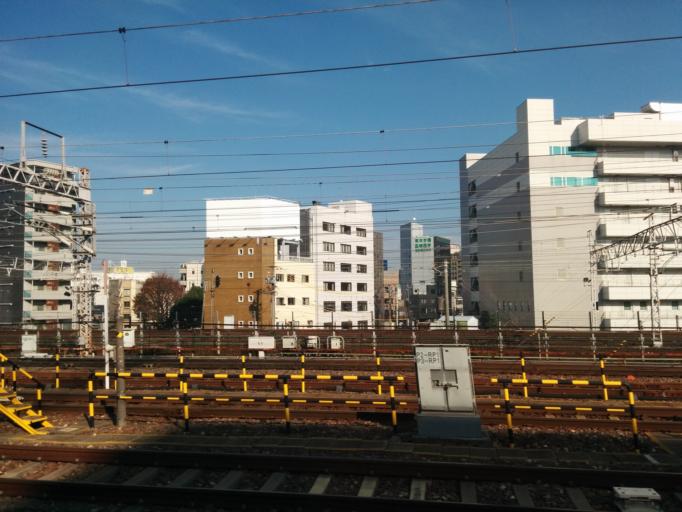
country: JP
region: Aichi
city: Nagoya-shi
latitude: 35.1768
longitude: 136.8783
